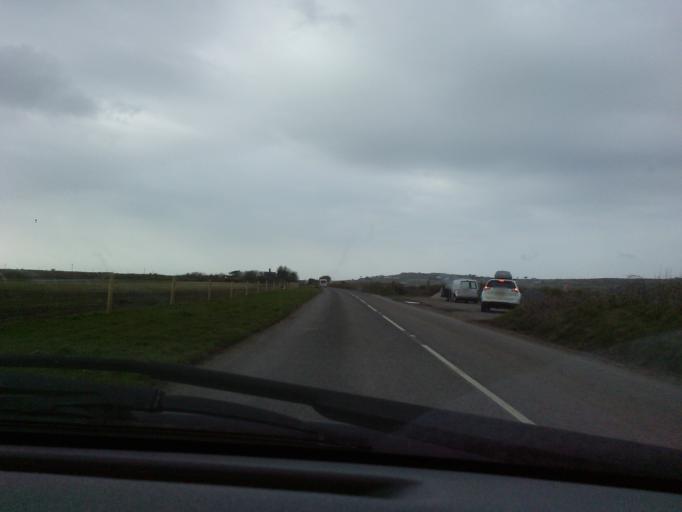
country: GB
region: England
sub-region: Cornwall
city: Saint Just
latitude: 50.1042
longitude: -5.6695
